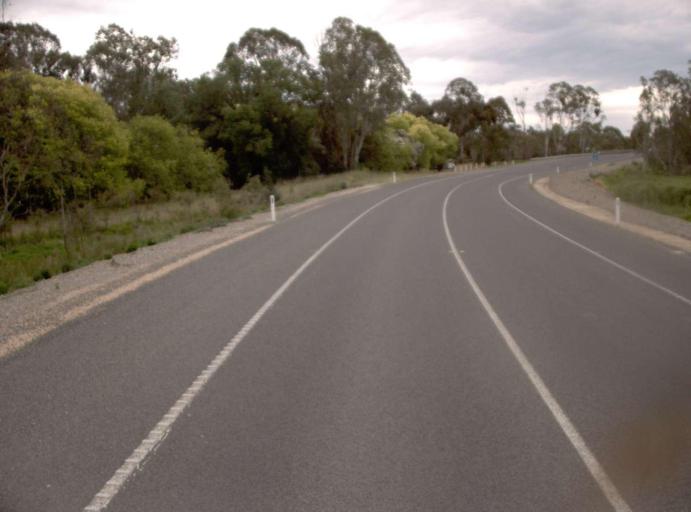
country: AU
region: Victoria
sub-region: Wellington
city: Sale
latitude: -38.1302
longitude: 147.0714
